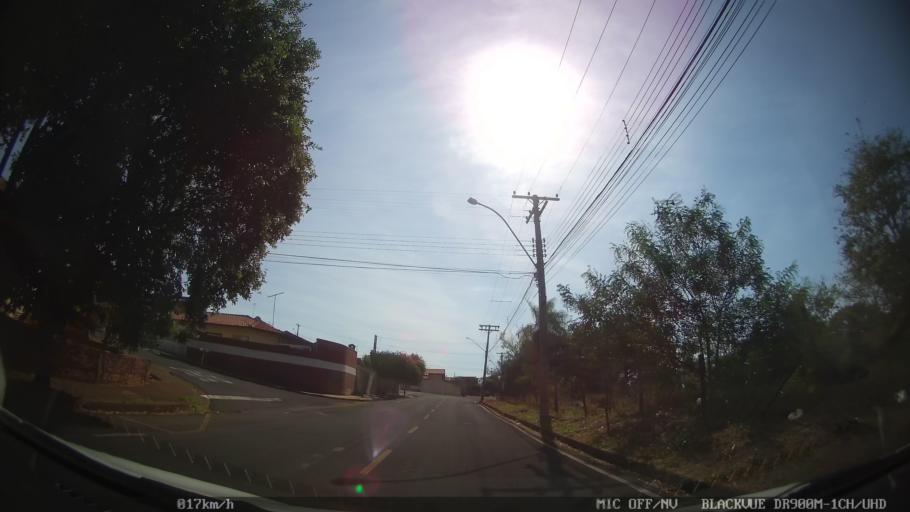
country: BR
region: Sao Paulo
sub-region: Sao Jose Do Rio Preto
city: Sao Jose do Rio Preto
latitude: -20.7865
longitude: -49.4303
